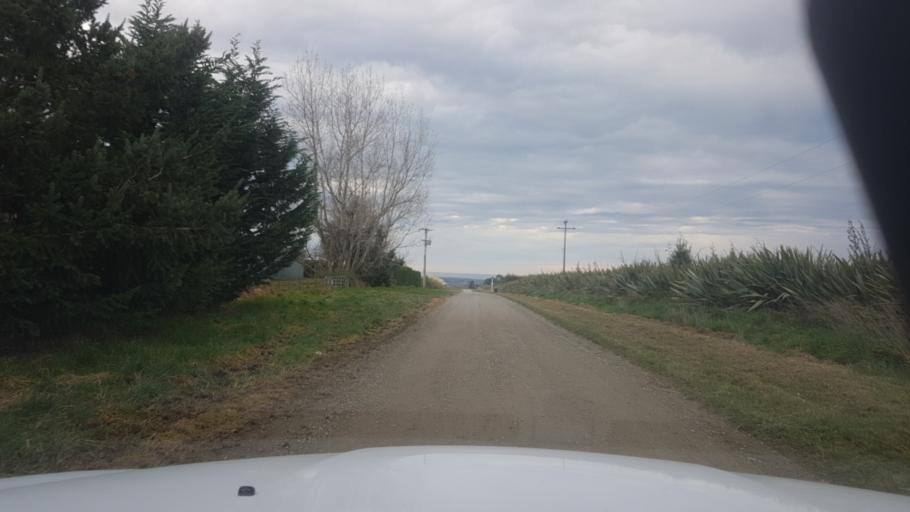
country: NZ
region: Canterbury
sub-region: Timaru District
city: Pleasant Point
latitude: -44.3460
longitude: 171.1217
